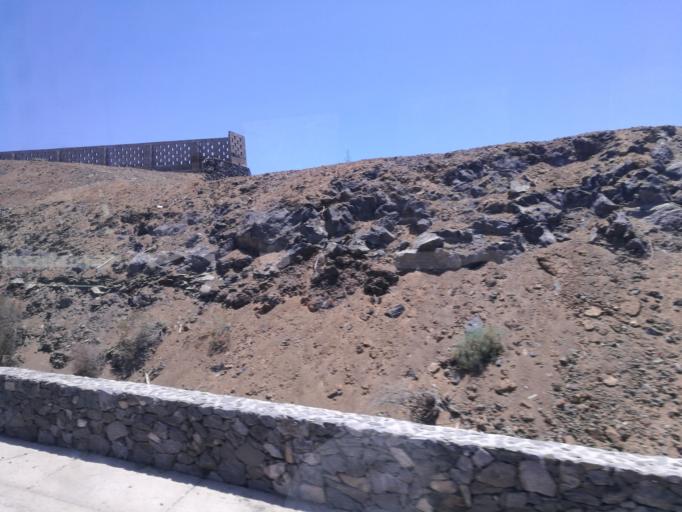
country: ES
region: Canary Islands
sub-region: Provincia de Santa Cruz de Tenerife
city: Guia de Isora
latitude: 28.1943
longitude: -16.8126
